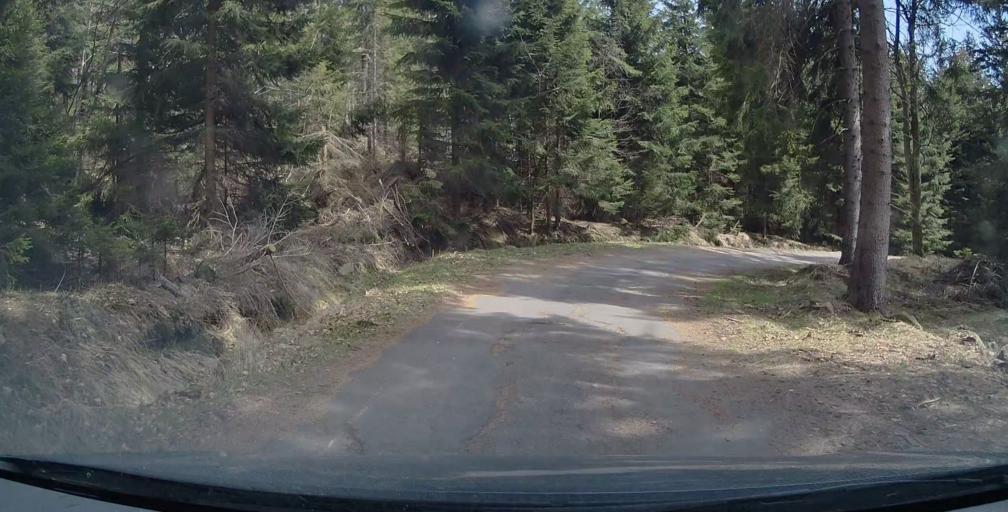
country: CZ
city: Machov
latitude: 50.4667
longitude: 16.2952
